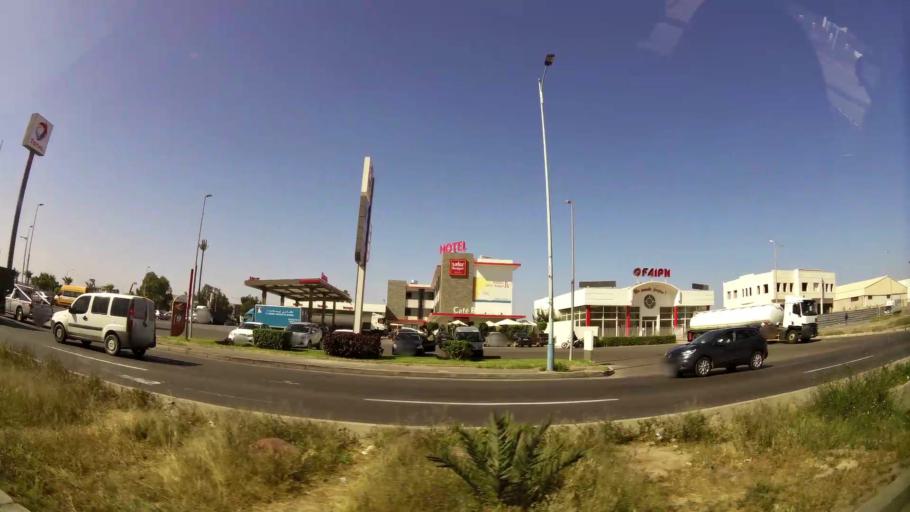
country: MA
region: Oued ed Dahab-Lagouira
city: Dakhla
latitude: 30.3975
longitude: -9.5236
